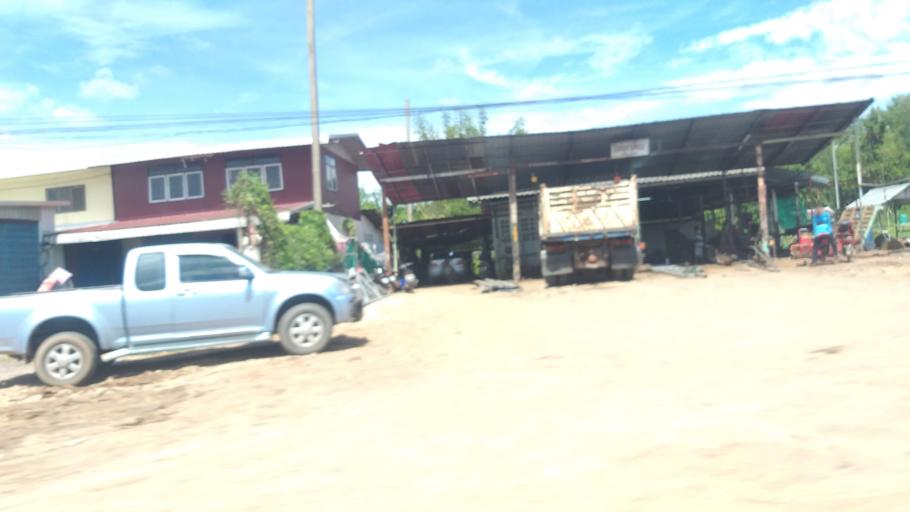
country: TH
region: Khon Kaen
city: Nong Ruea
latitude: 16.4846
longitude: 102.4359
